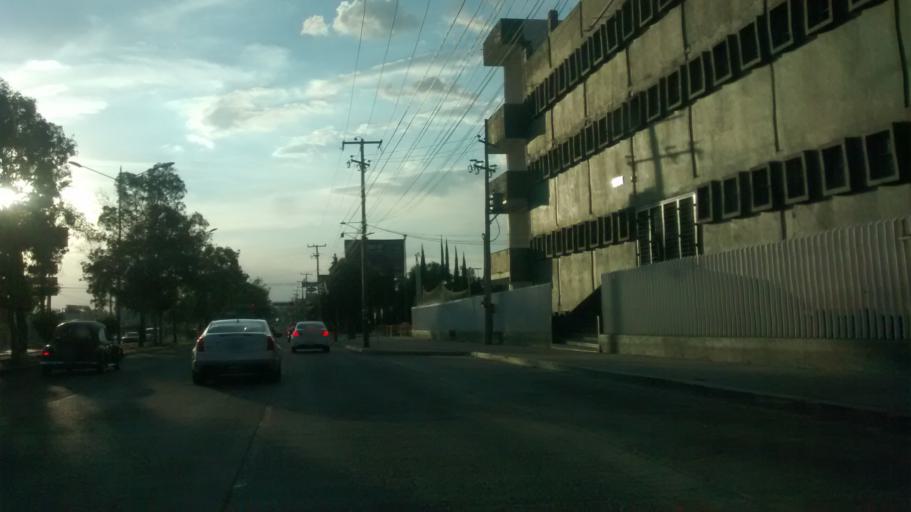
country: MX
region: Guanajuato
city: Leon
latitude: 21.0975
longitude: -101.6568
